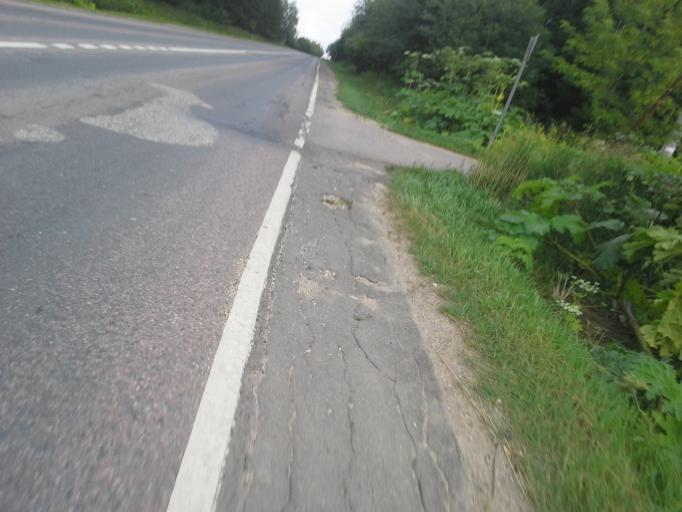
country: RU
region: Moskovskaya
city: Istra
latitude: 55.9318
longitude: 36.9266
